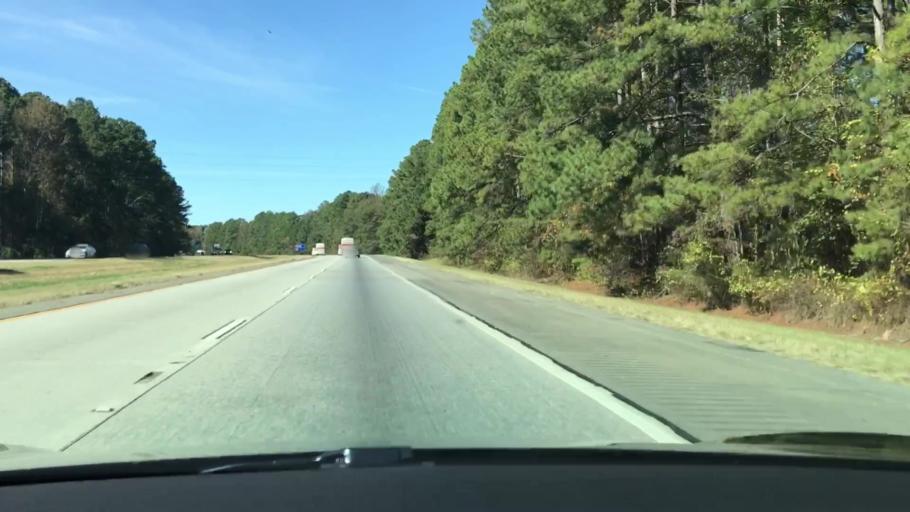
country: US
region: Georgia
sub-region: Greene County
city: Union Point
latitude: 33.5497
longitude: -83.0517
